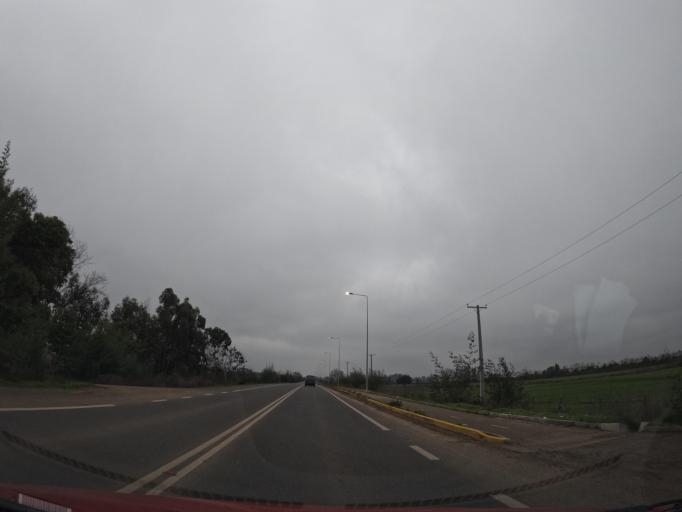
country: CL
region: Maule
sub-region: Provincia de Talca
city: San Clemente
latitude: -35.5329
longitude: -71.4741
